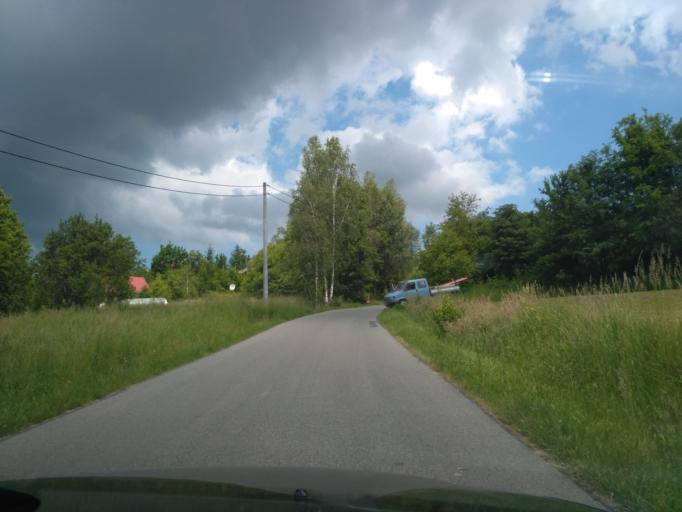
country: PL
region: Subcarpathian Voivodeship
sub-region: Powiat rzeszowski
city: Hyzne
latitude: 49.9334
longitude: 22.1712
